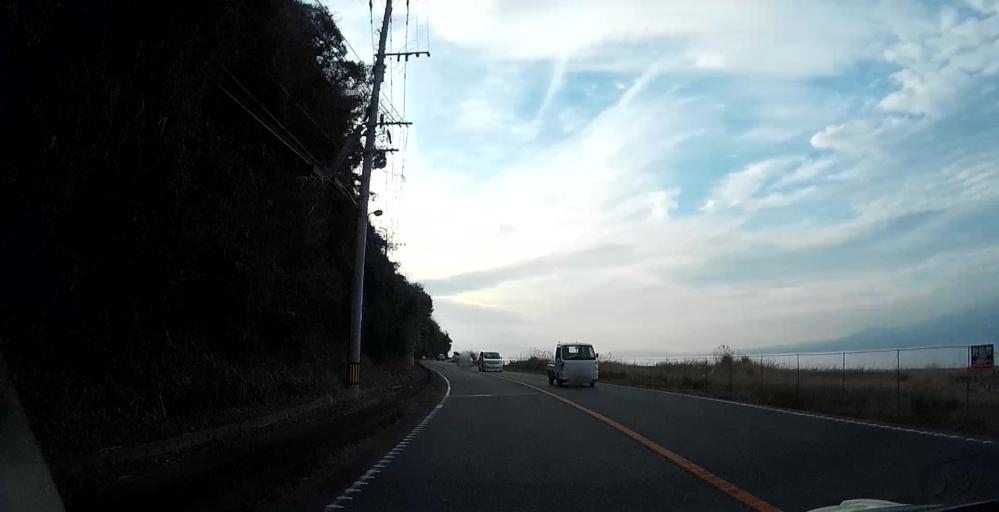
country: JP
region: Kumamoto
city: Matsubase
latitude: 32.6455
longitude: 130.4855
